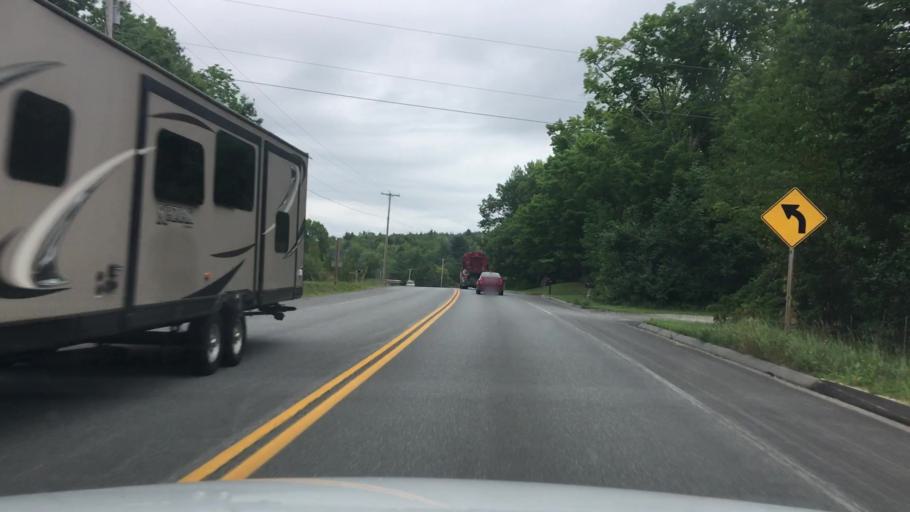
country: US
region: Maine
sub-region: Hancock County
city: Franklin
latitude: 44.8390
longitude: -68.3478
